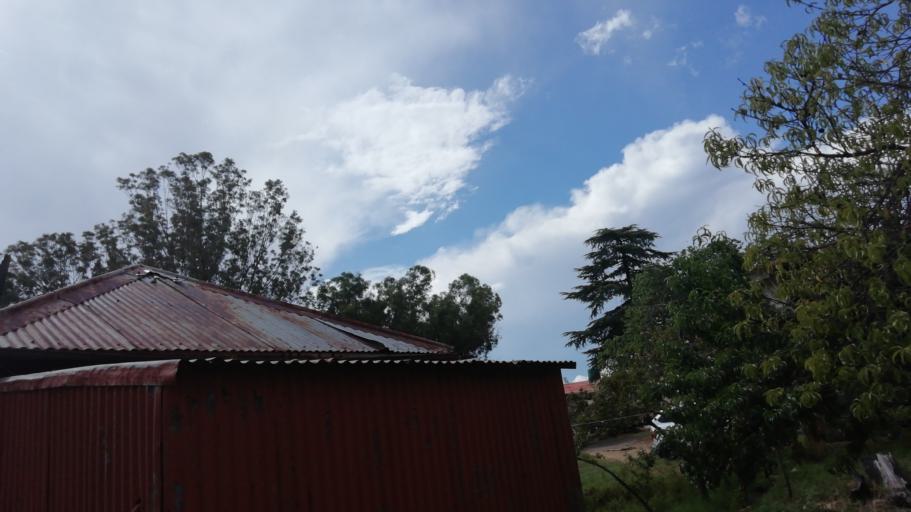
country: LS
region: Maseru
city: Nako
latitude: -29.6315
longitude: 27.5008
